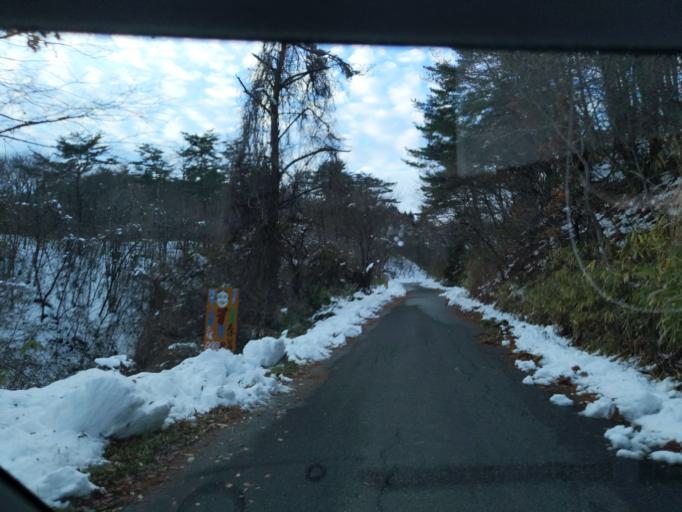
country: JP
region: Iwate
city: Mizusawa
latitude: 39.0414
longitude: 141.0287
